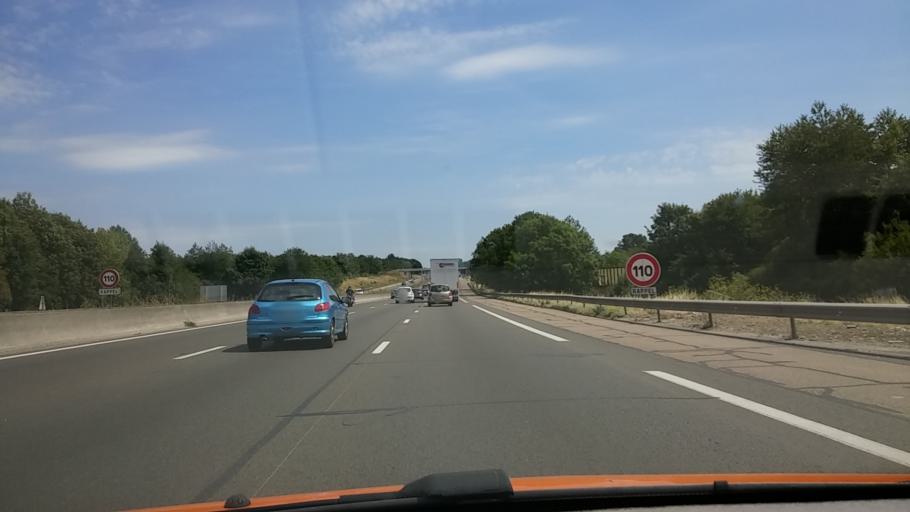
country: FR
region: Ile-de-France
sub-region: Departement de Seine-et-Marne
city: Champs-sur-Marne
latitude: 48.8337
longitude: 2.5909
